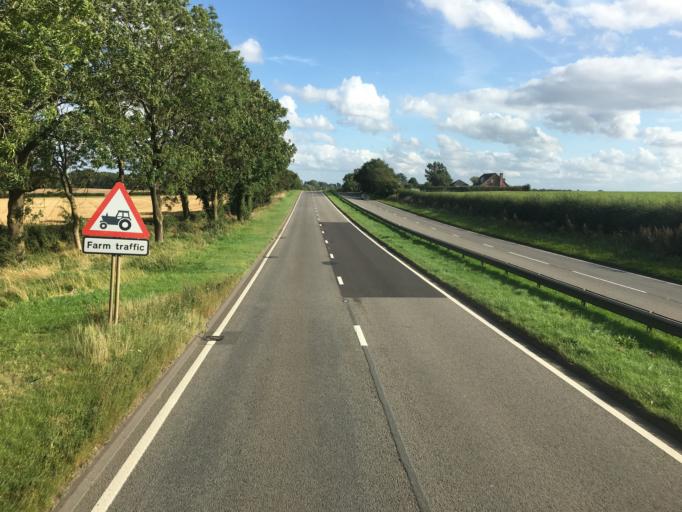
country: GB
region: England
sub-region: Leicestershire
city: Lutterworth
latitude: 52.4417
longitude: -1.2436
